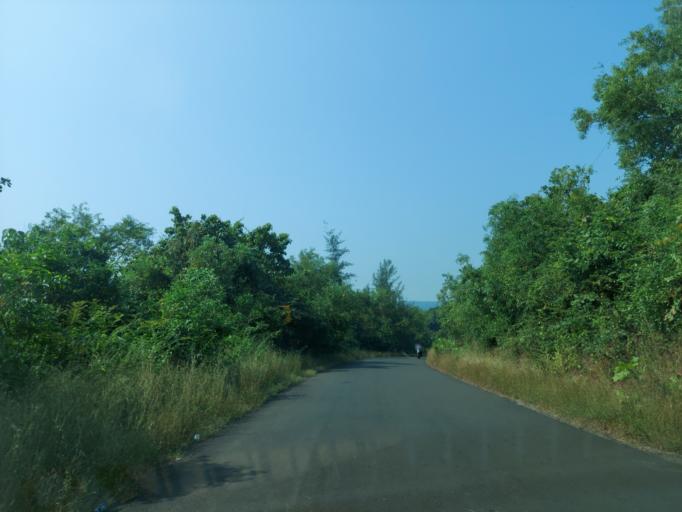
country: IN
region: Maharashtra
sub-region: Sindhudurg
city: Kudal
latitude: 15.9717
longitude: 73.6455
